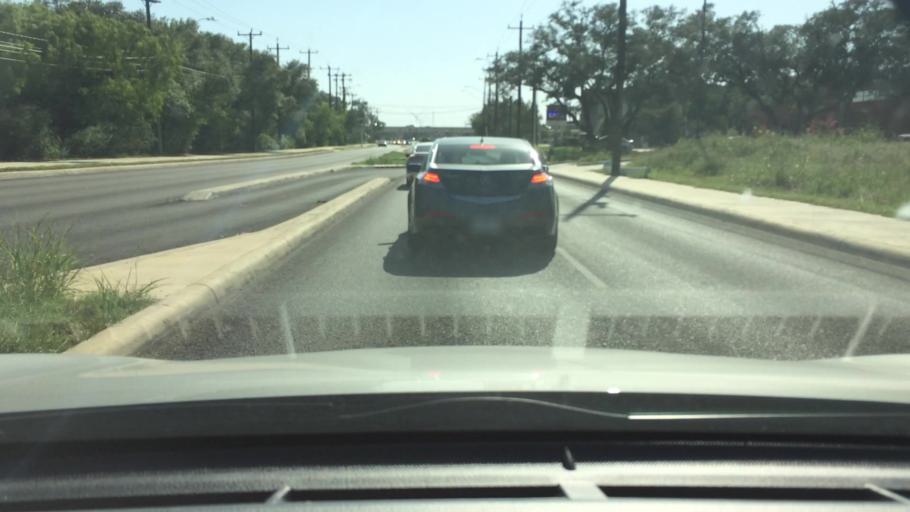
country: US
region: Texas
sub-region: Bexar County
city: Helotes
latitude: 29.5706
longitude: -98.6472
